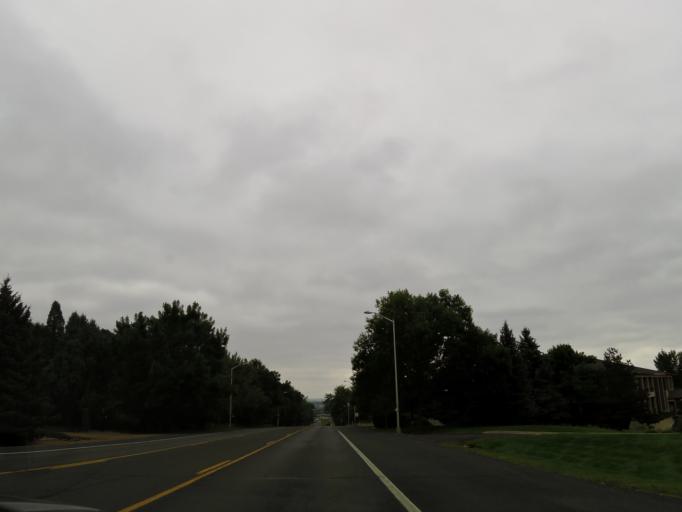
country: US
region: Colorado
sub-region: El Paso County
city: Colorado Springs
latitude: 38.7951
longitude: -104.8321
